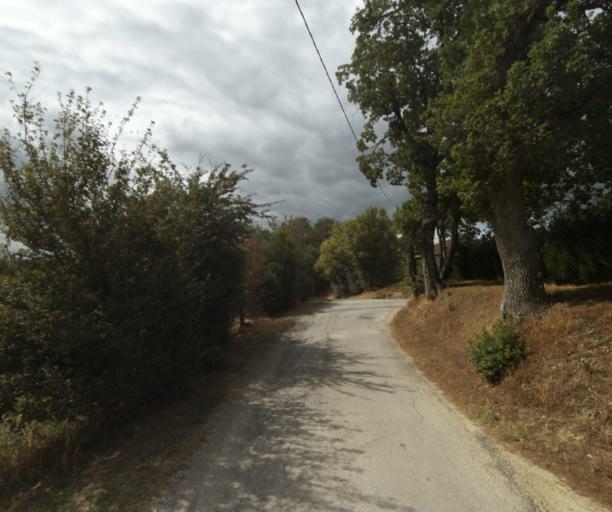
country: FR
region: Midi-Pyrenees
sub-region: Departement du Tarn
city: Soreze
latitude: 43.4626
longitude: 2.0641
